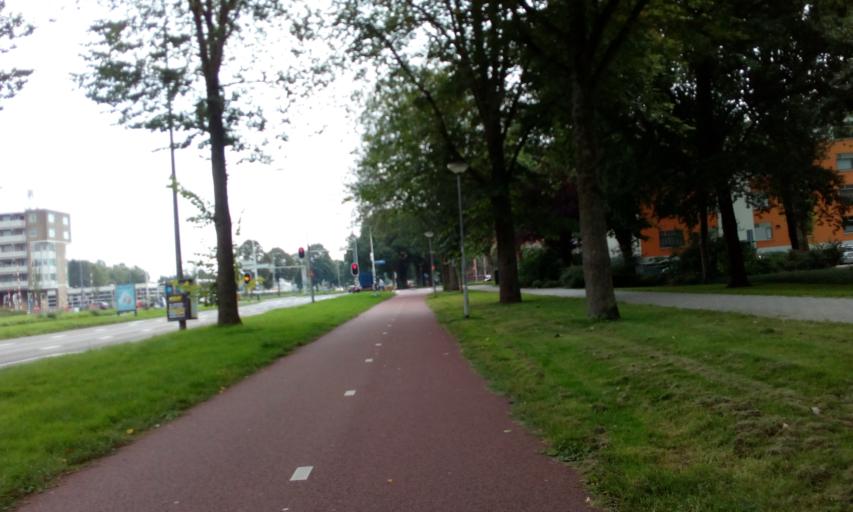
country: NL
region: South Holland
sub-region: Gemeente Rotterdam
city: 's-Gravenland
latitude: 51.9416
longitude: 4.5554
